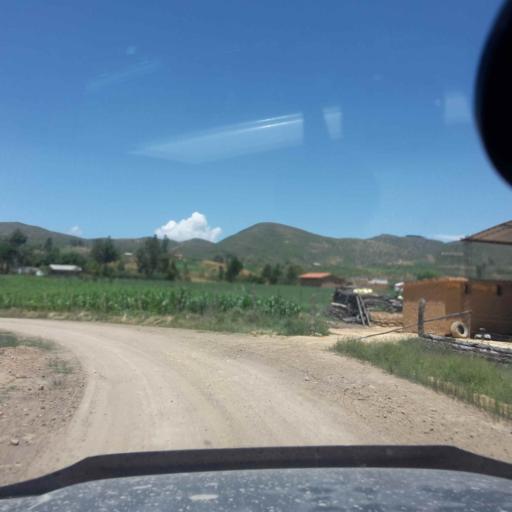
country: BO
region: Cochabamba
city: Totora
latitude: -17.7744
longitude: -65.2571
